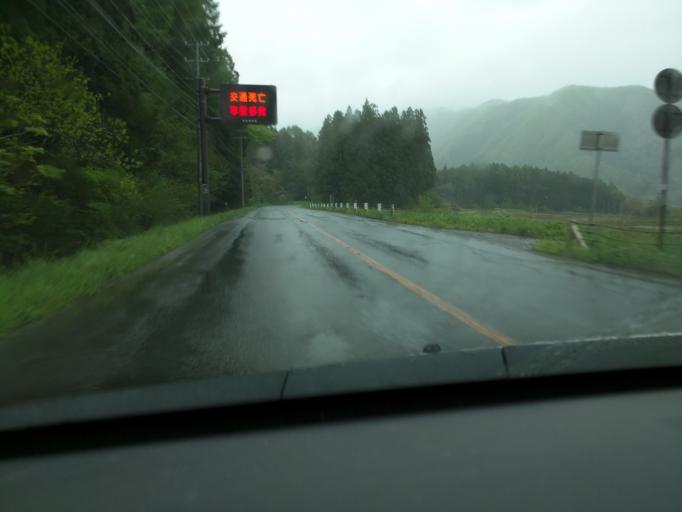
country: JP
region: Fukushima
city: Inawashiro
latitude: 37.5996
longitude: 140.1252
